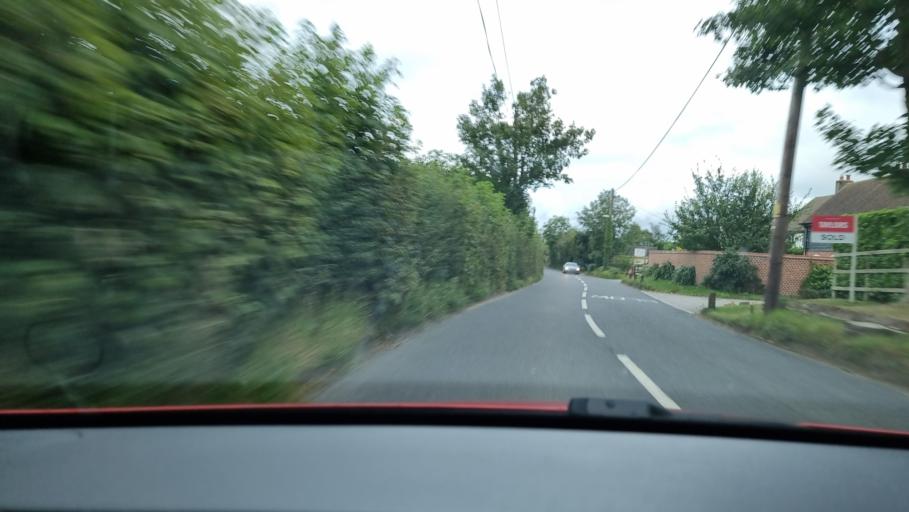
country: GB
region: England
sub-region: Buckinghamshire
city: Cheddington
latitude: 51.8650
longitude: -0.6586
